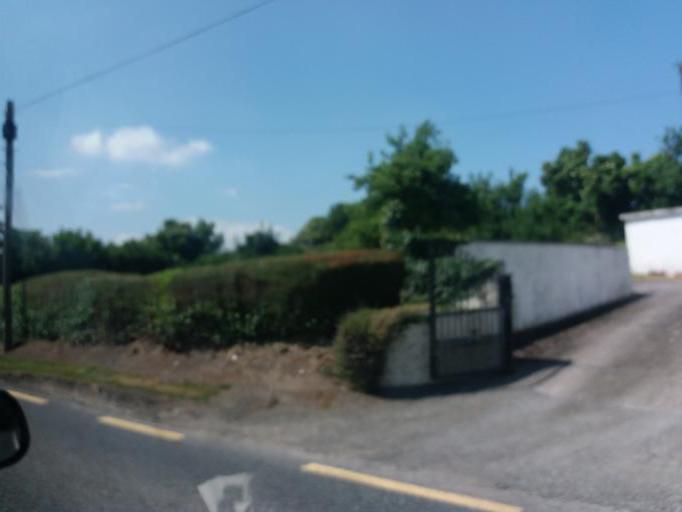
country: IE
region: Leinster
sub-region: An Mhi
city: Slane
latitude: 53.7070
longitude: -6.5286
